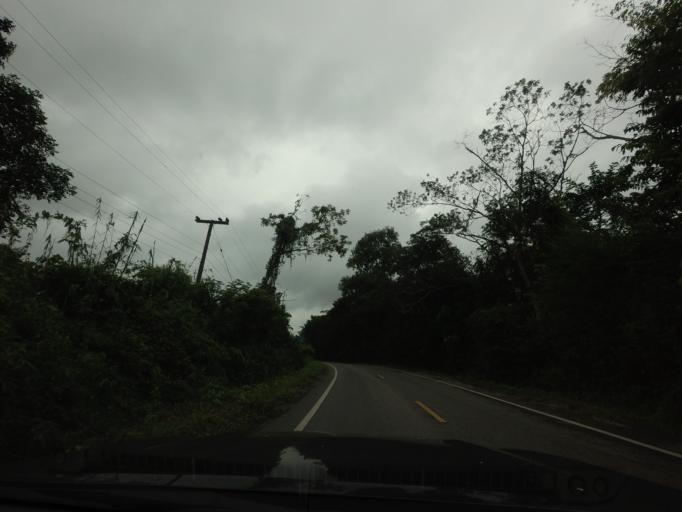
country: TH
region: Nong Khai
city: Sangkhom
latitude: 18.0263
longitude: 102.3563
